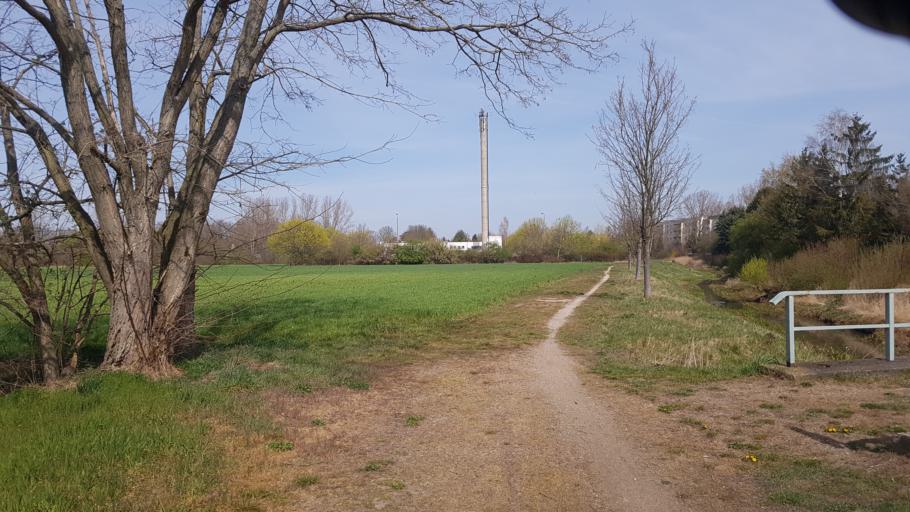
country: DE
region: Brandenburg
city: Doberlug-Kirchhain
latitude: 51.6310
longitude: 13.5552
